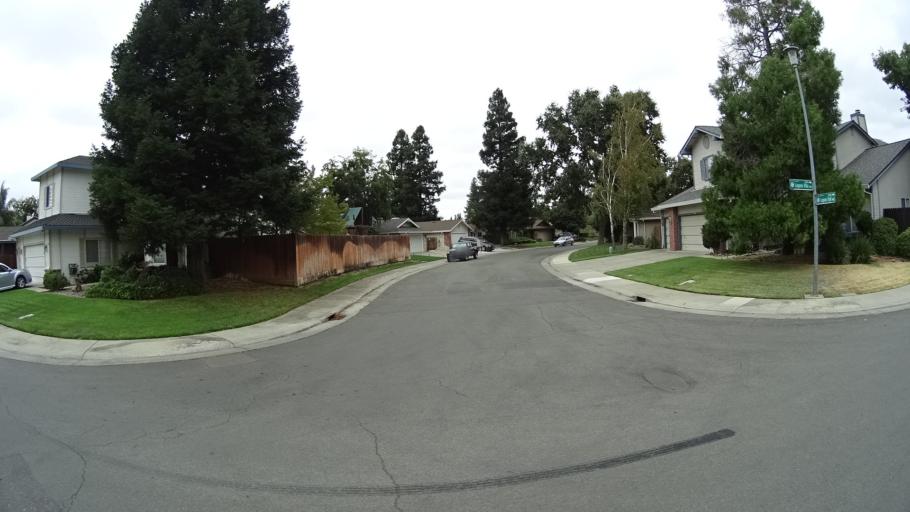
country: US
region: California
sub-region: Sacramento County
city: Laguna
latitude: 38.4205
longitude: -121.4359
